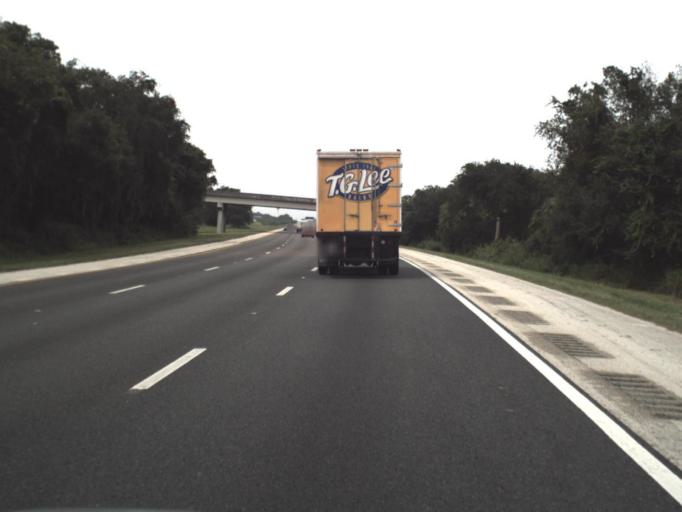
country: US
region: Florida
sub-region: Manatee County
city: Ellenton
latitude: 27.5021
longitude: -82.4794
